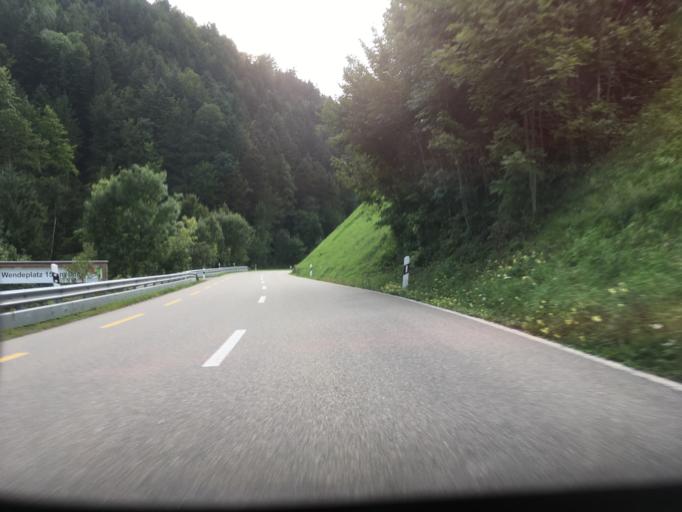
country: CH
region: Thurgau
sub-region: Muenchwilen District
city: Fischingen
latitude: 47.3491
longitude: 8.9512
